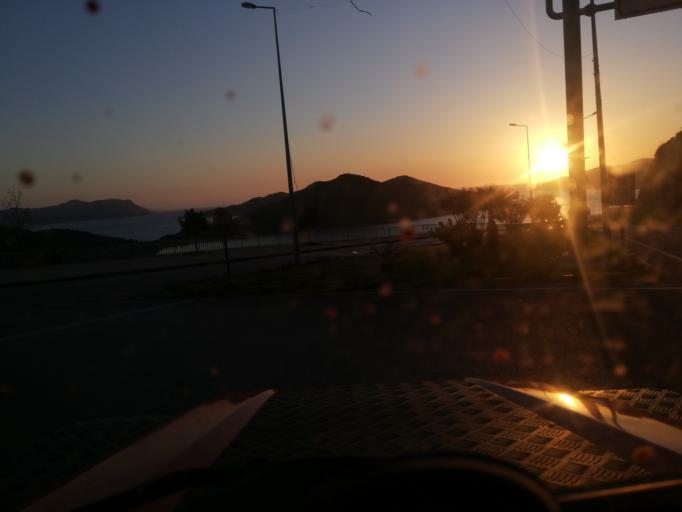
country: TR
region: Antalya
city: Kas
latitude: 36.2071
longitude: 29.6320
